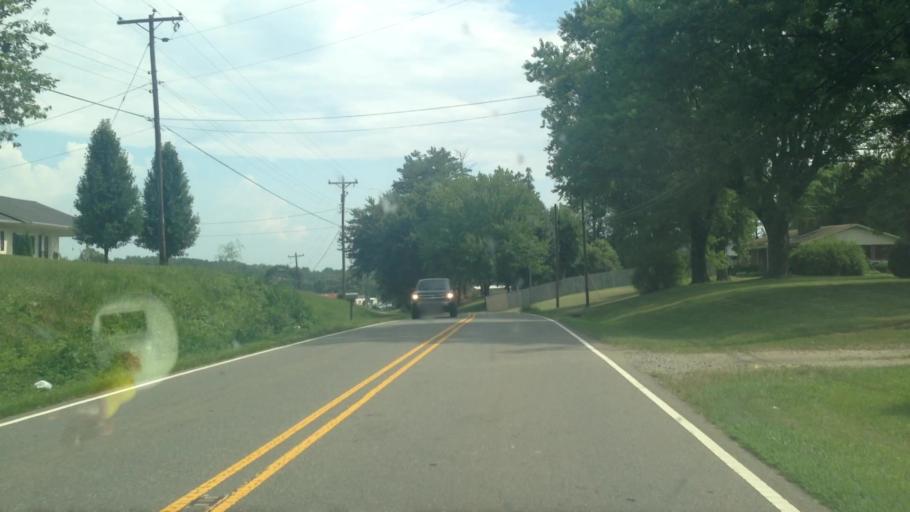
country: US
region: North Carolina
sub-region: Surry County
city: Flat Rock
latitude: 36.4742
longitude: -80.5744
